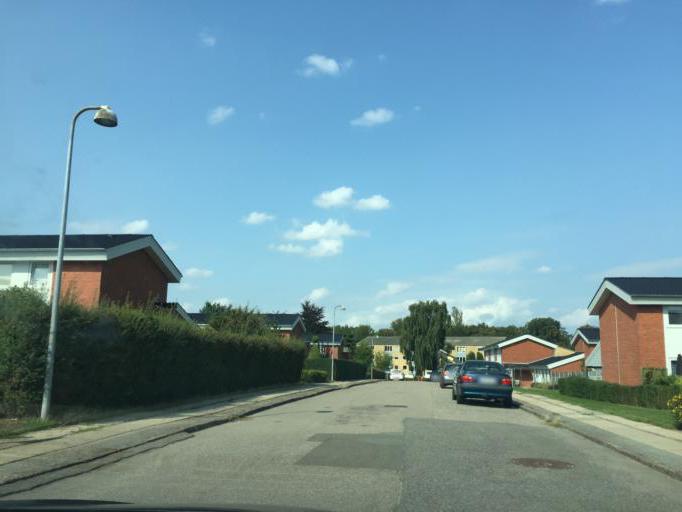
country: DK
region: South Denmark
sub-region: Odense Kommune
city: Odense
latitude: 55.4004
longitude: 10.3444
